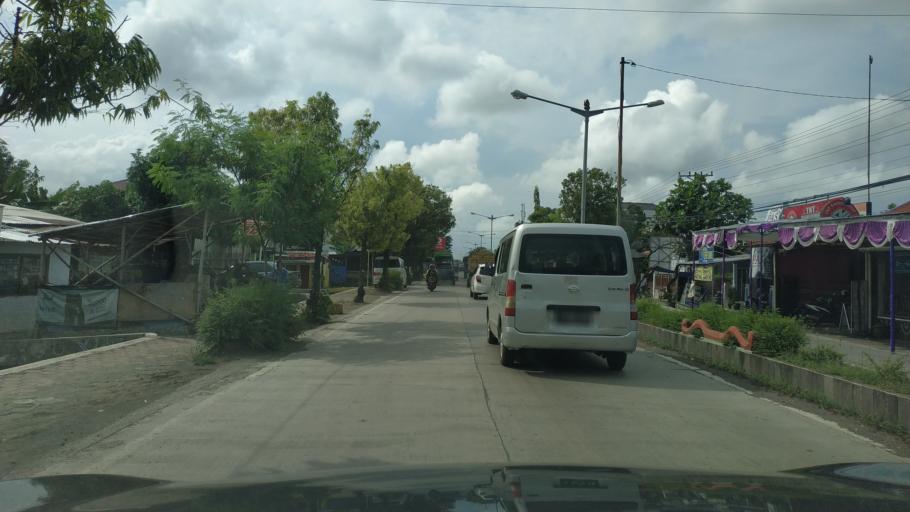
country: ID
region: Central Java
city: Pemalang
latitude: -6.9129
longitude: 109.3826
